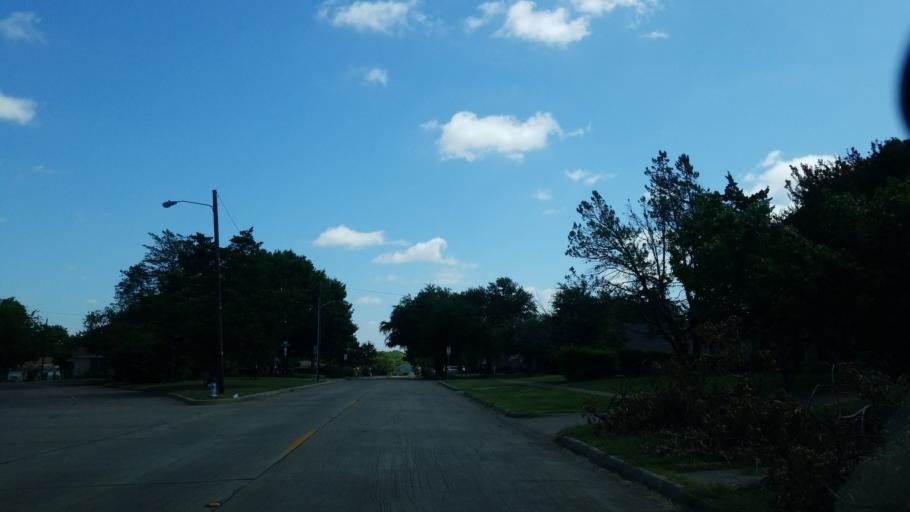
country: US
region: Texas
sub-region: Dallas County
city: Dallas
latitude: 32.7286
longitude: -96.7957
